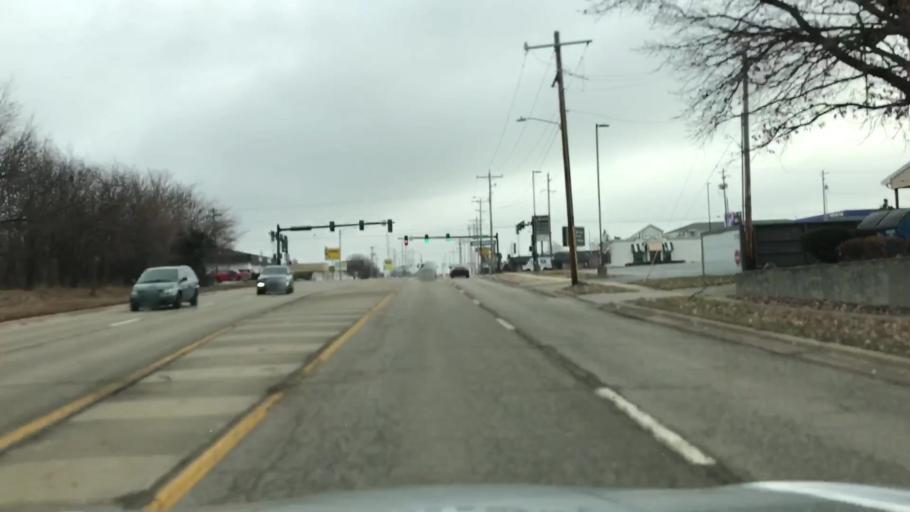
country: US
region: Illinois
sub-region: McLean County
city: Normal
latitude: 40.5027
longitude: -88.9589
